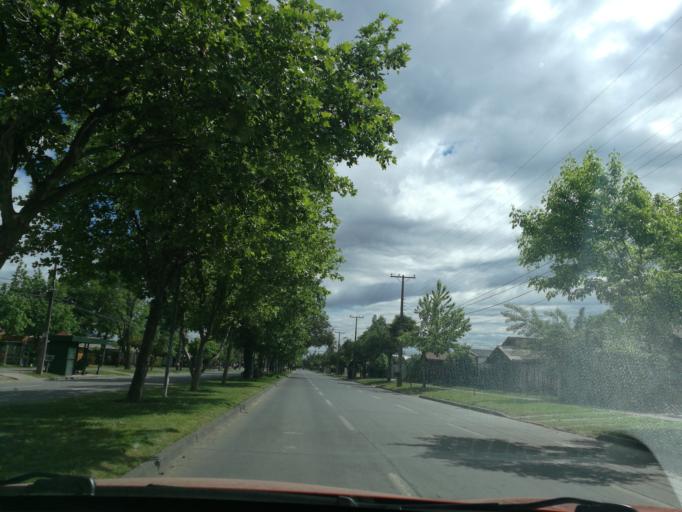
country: CL
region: O'Higgins
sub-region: Provincia de Cachapoal
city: Rancagua
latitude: -34.1560
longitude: -70.7323
